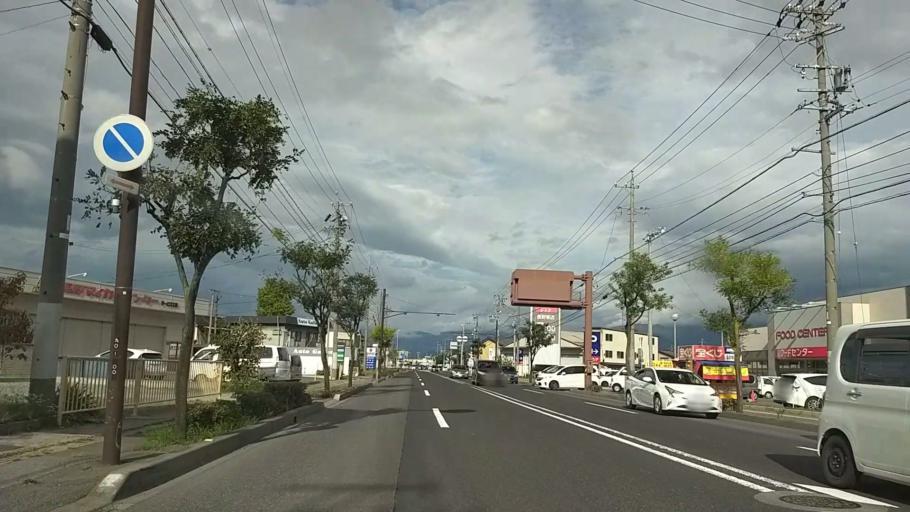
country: JP
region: Nagano
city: Suzaka
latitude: 36.6582
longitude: 138.2526
